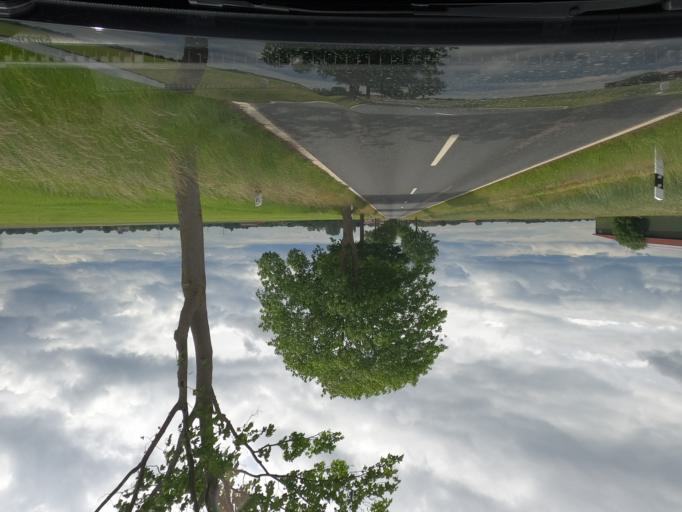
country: DE
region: Lower Saxony
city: Lehrte
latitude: 52.4198
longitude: 9.9613
